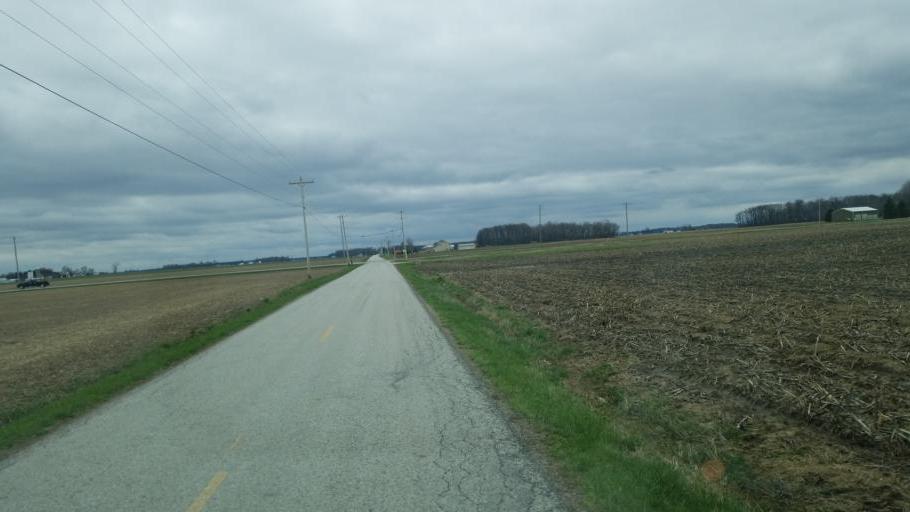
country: US
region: Ohio
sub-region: Marion County
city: Prospect
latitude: 40.3869
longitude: -83.1185
